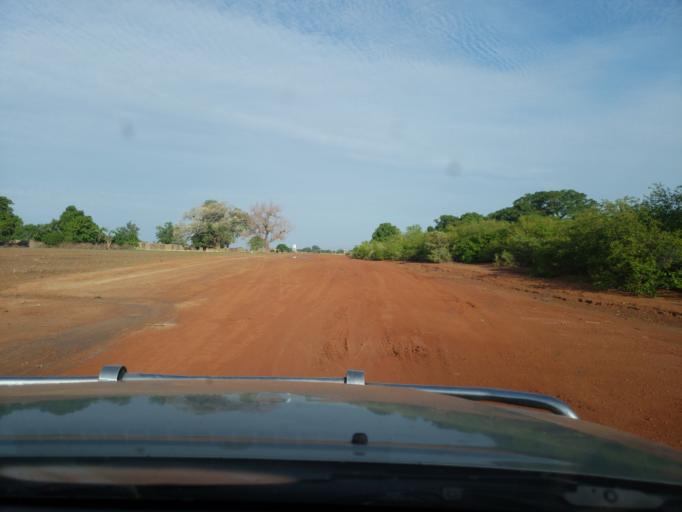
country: ML
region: Sikasso
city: Koutiala
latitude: 12.4238
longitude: -5.6683
